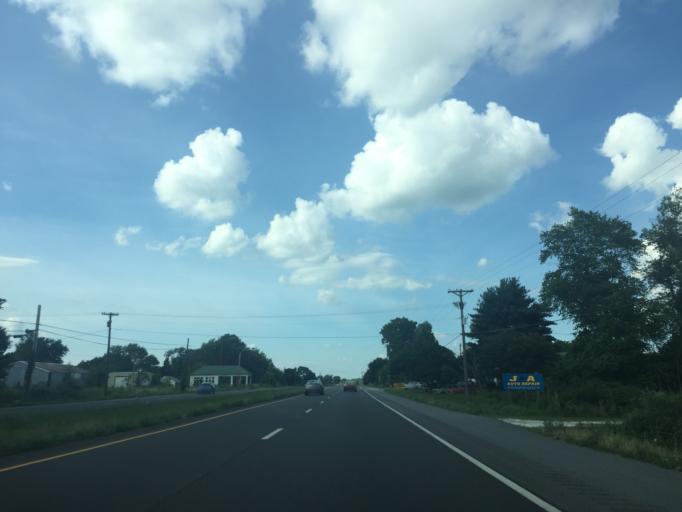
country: US
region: Delaware
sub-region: Sussex County
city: Bridgeville
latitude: 38.7937
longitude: -75.5896
